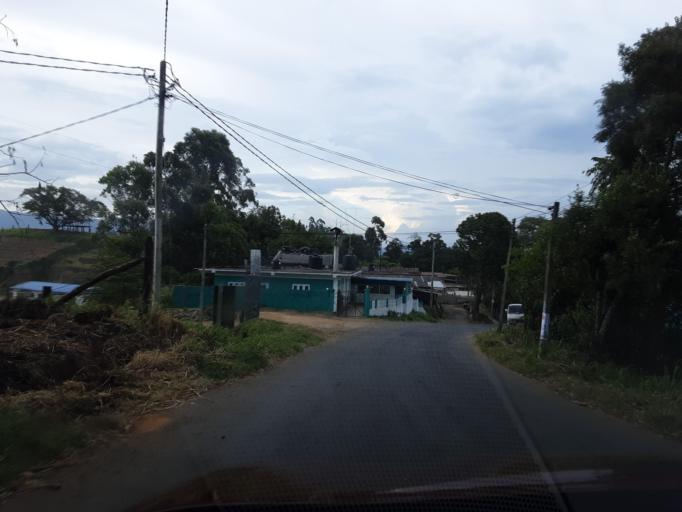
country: LK
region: Uva
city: Haputale
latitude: 6.8912
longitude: 80.9156
